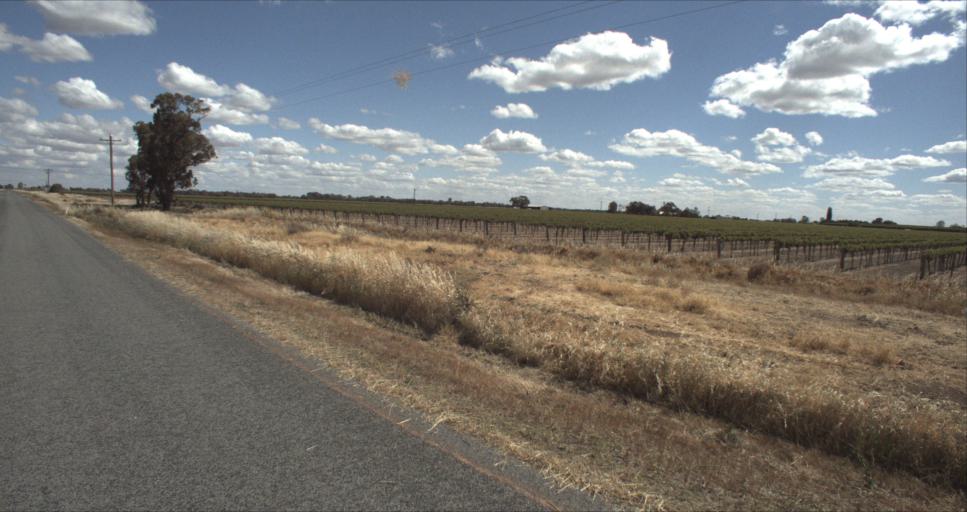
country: AU
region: New South Wales
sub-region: Leeton
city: Leeton
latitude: -34.4929
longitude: 146.2469
